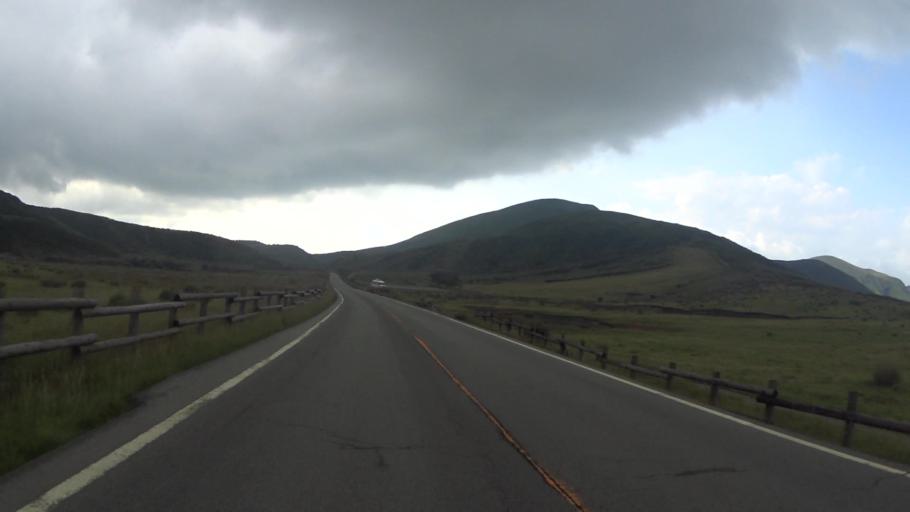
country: JP
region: Kumamoto
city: Aso
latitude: 32.8827
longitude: 131.0673
